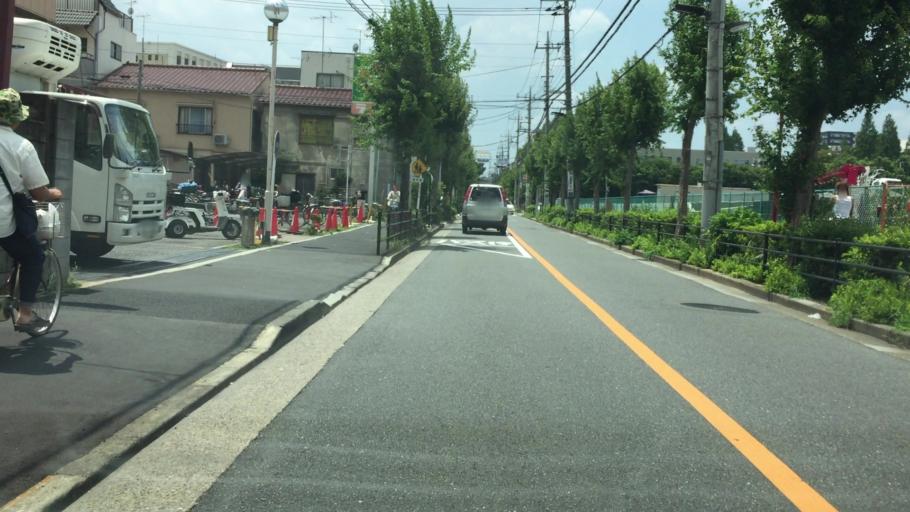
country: JP
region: Saitama
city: Soka
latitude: 35.7496
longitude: 139.7756
